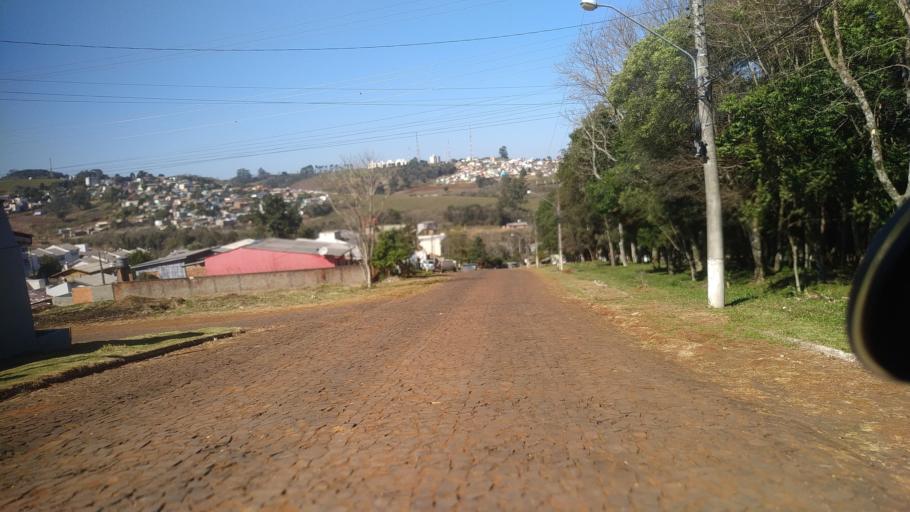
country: BR
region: Santa Catarina
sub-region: Chapeco
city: Chapeco
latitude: -27.0913
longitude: -52.5874
